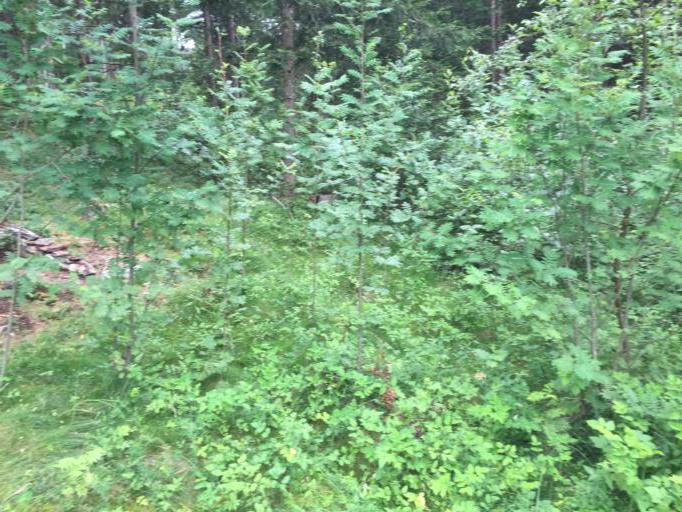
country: IT
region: Trentino-Alto Adige
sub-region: Bolzano
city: Falzes
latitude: 46.8079
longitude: 11.8754
